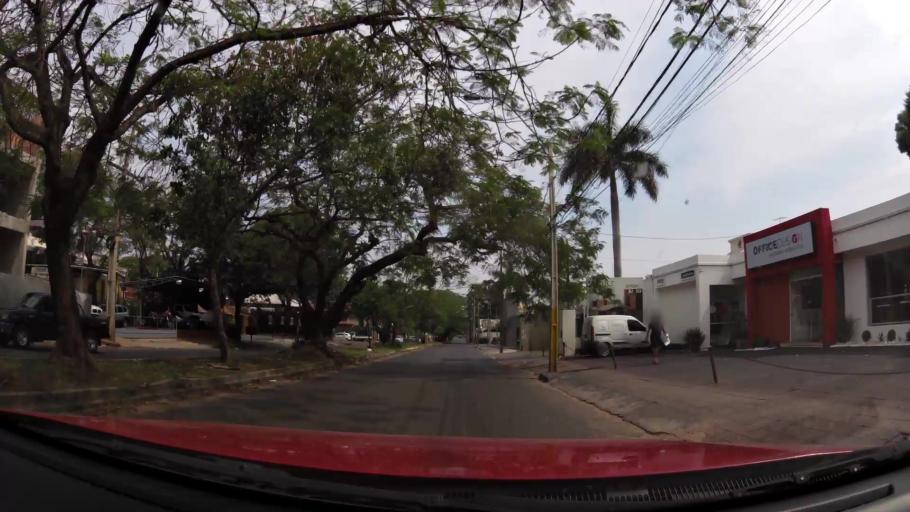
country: PY
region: Asuncion
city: Asuncion
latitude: -25.2825
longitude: -57.5713
